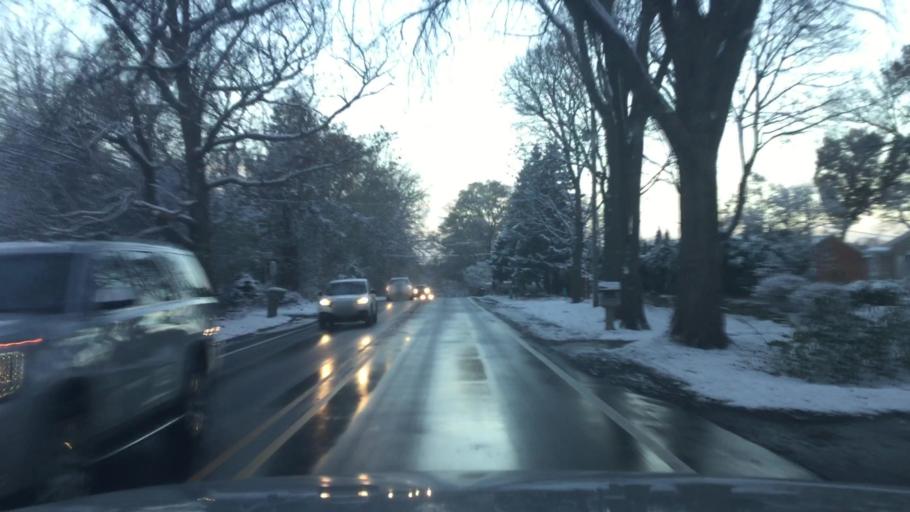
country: US
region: Michigan
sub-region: Oakland County
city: West Bloomfield Township
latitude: 42.5895
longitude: -83.4201
